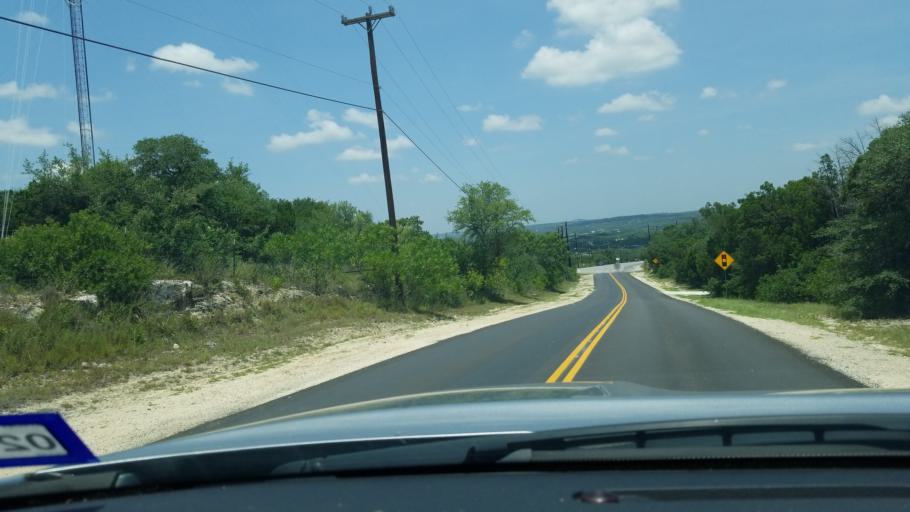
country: US
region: Texas
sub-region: Bexar County
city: Timberwood Park
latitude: 29.7117
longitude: -98.4548
